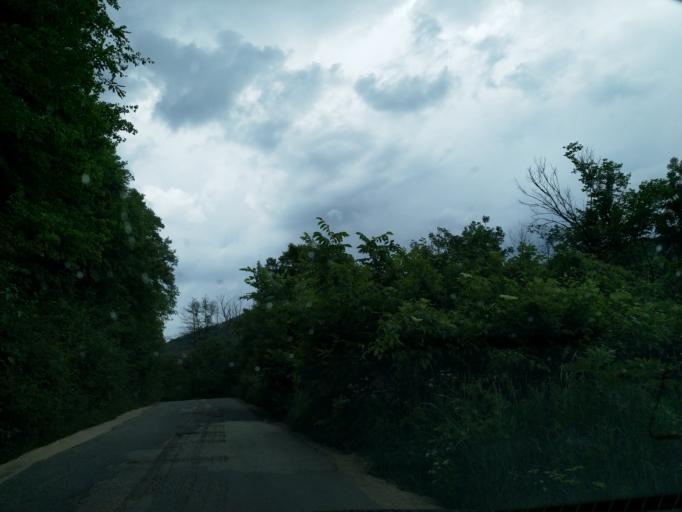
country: RS
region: Central Serbia
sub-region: Borski Okrug
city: Bor
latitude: 44.0233
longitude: 21.9781
